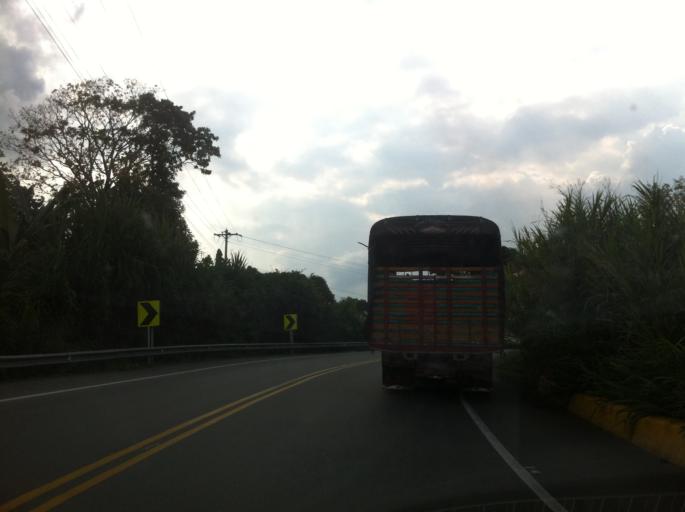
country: CO
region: Quindio
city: La Tebaida
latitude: 4.4459
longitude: -75.8264
